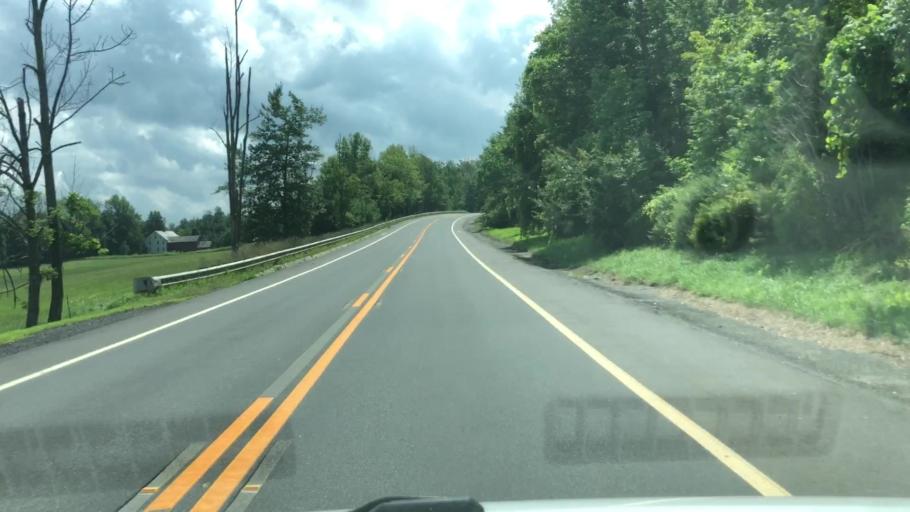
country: US
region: Massachusetts
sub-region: Franklin County
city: Ashfield
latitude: 42.5199
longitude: -72.8068
